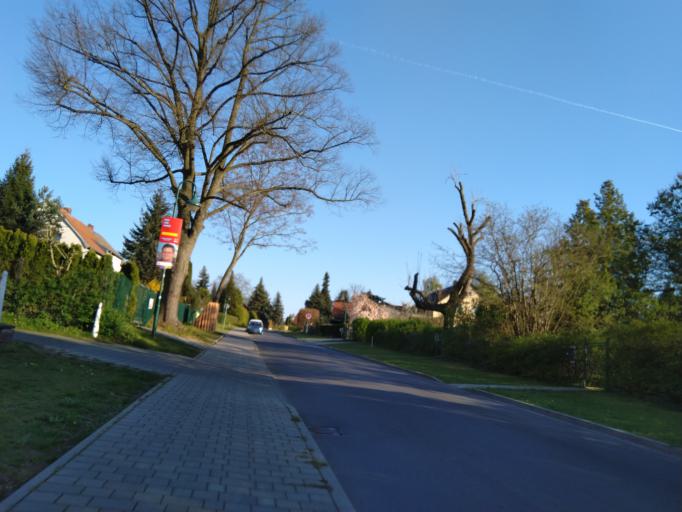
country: DE
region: Berlin
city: Buch
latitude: 52.6447
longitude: 13.5247
